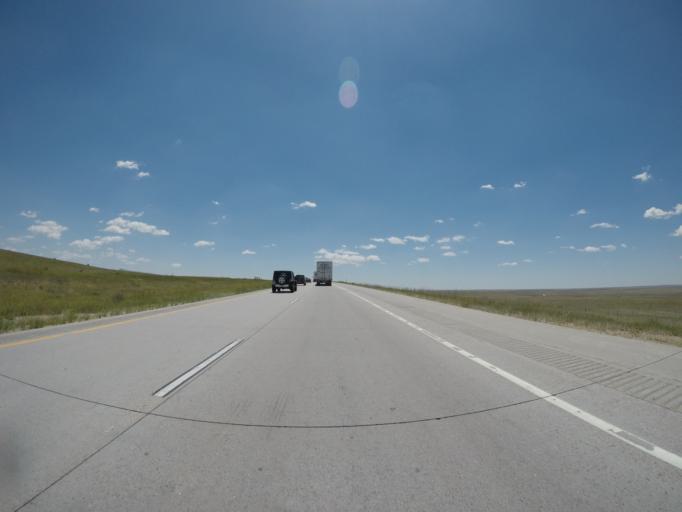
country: US
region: Colorado
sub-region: Lincoln County
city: Limon
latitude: 39.3597
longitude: -103.8751
